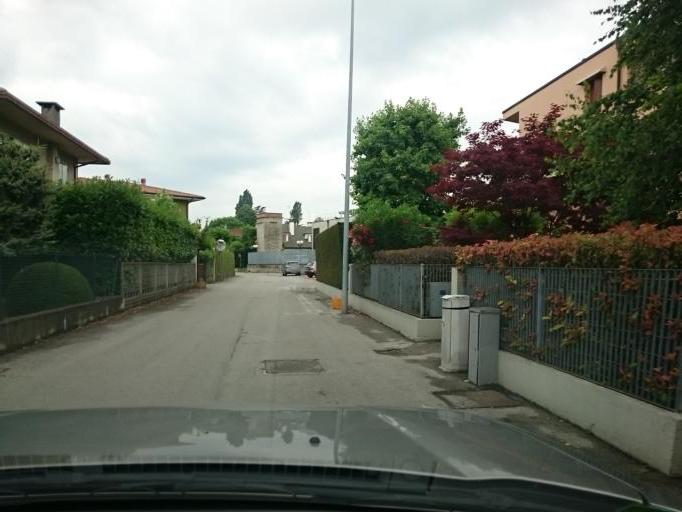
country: IT
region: Veneto
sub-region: Provincia di Padova
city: Mandriola-Sant'Agostino
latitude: 45.3767
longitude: 11.8545
